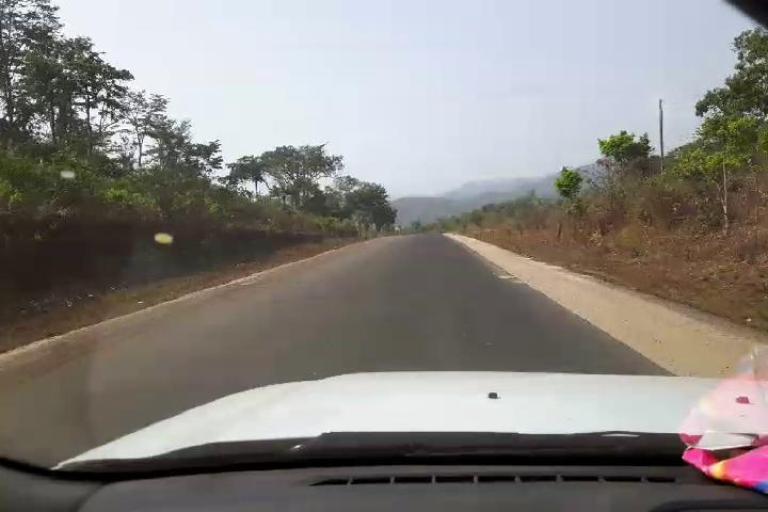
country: SL
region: Western Area
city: Waterloo
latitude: 8.2663
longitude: -13.1605
